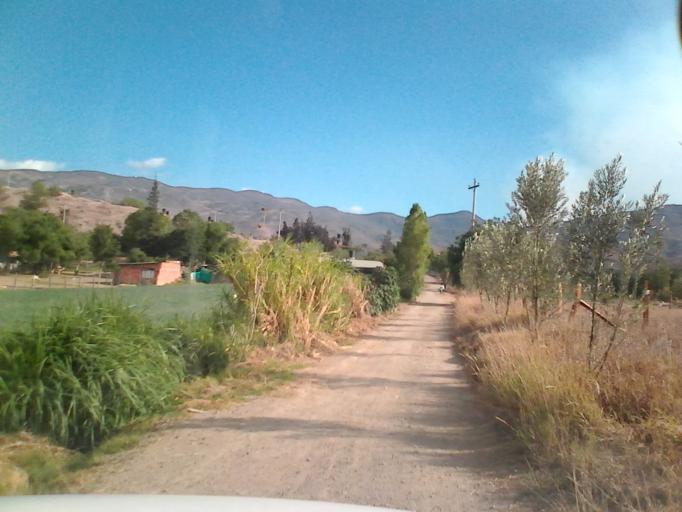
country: CO
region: Boyaca
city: Sachica
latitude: 5.5885
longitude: -73.5471
